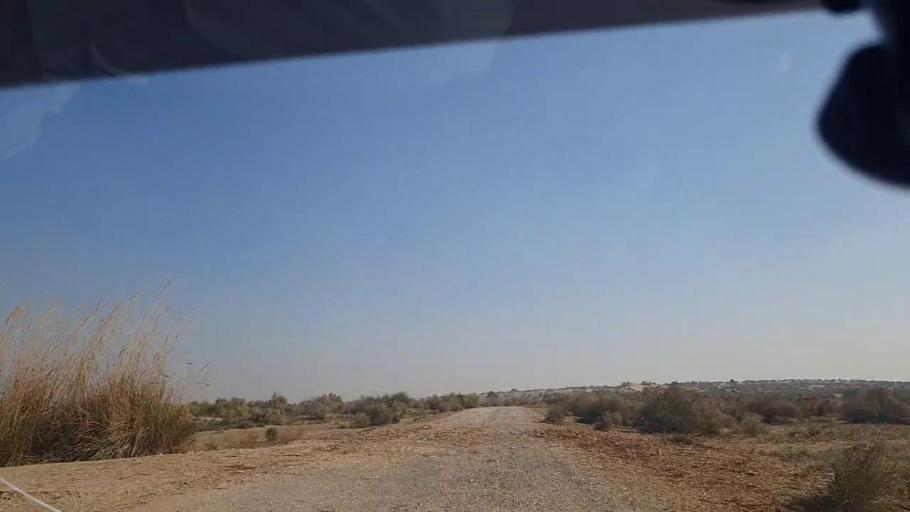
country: PK
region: Sindh
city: Khanpur
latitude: 27.5623
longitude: 69.3228
